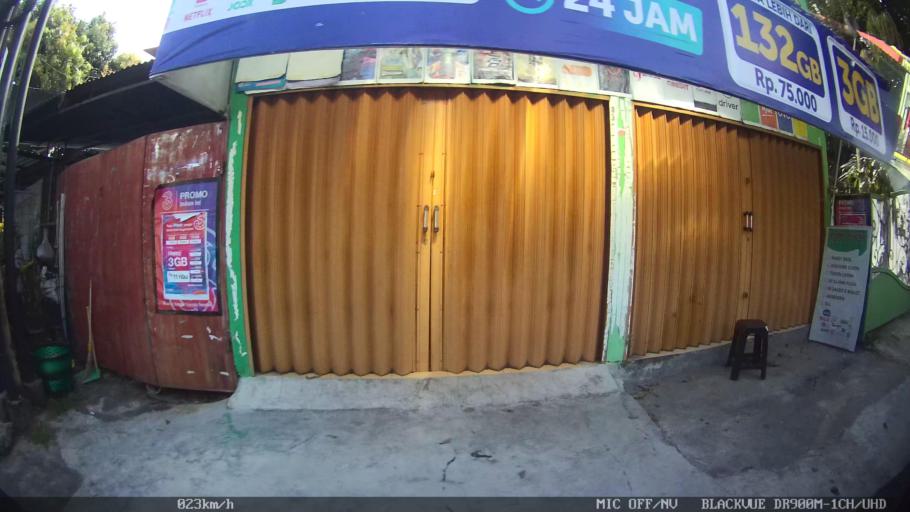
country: ID
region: Daerah Istimewa Yogyakarta
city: Depok
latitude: -7.7535
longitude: 110.4416
